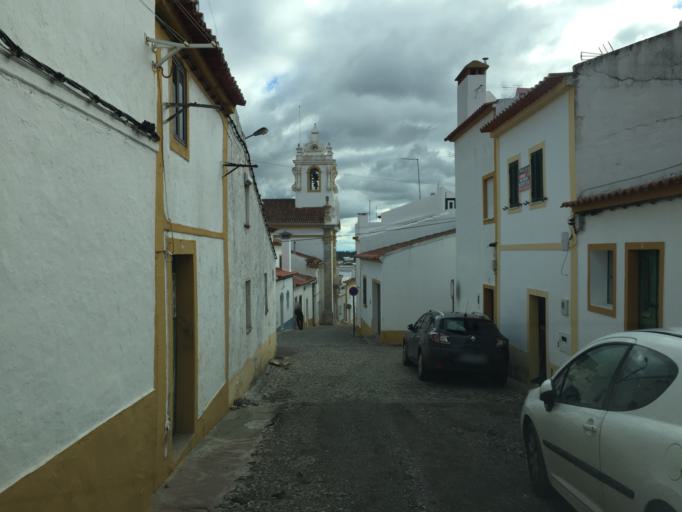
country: PT
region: Portalegre
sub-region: Alter do Chao
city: Alter do Chao
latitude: 39.2018
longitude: -7.6591
